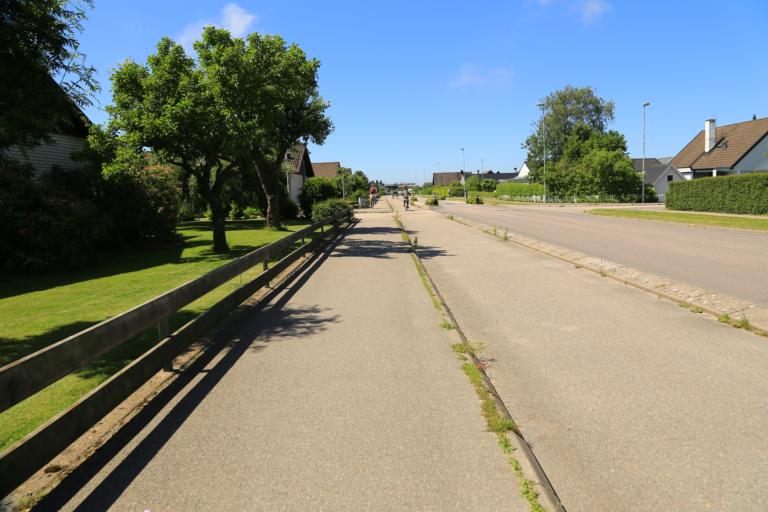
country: SE
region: Halland
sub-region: Varbergs Kommun
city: Varberg
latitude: 57.1060
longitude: 12.2782
